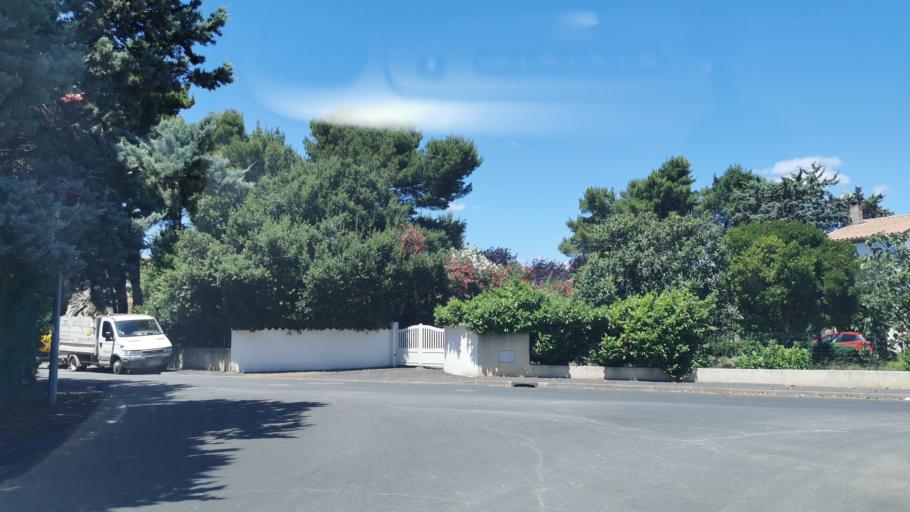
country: FR
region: Languedoc-Roussillon
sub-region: Departement de l'Aude
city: Narbonne
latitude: 43.1864
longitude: 3.0303
